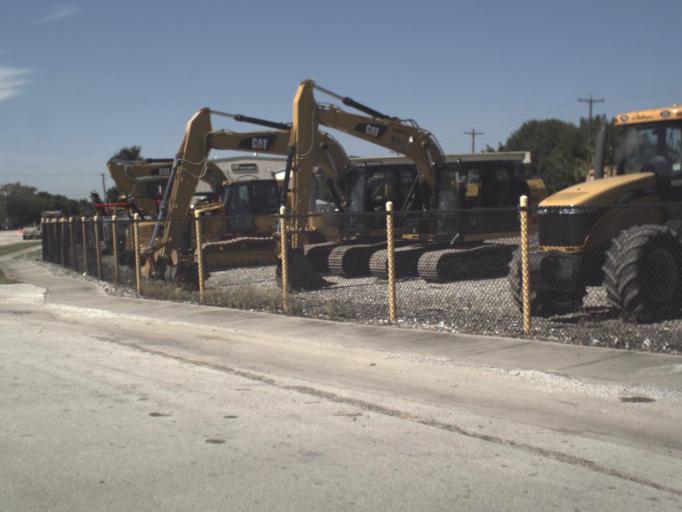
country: US
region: Florida
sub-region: Hendry County
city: Clewiston
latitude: 26.7544
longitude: -80.9204
